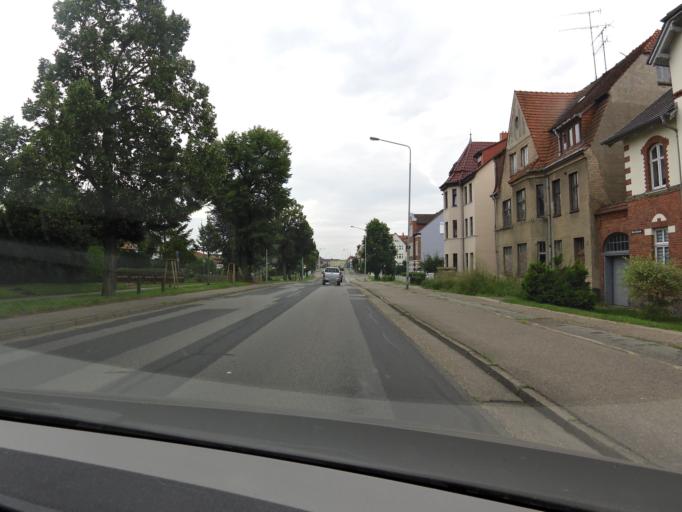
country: DE
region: Mecklenburg-Vorpommern
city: Neustrelitz
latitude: 53.3379
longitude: 13.0883
